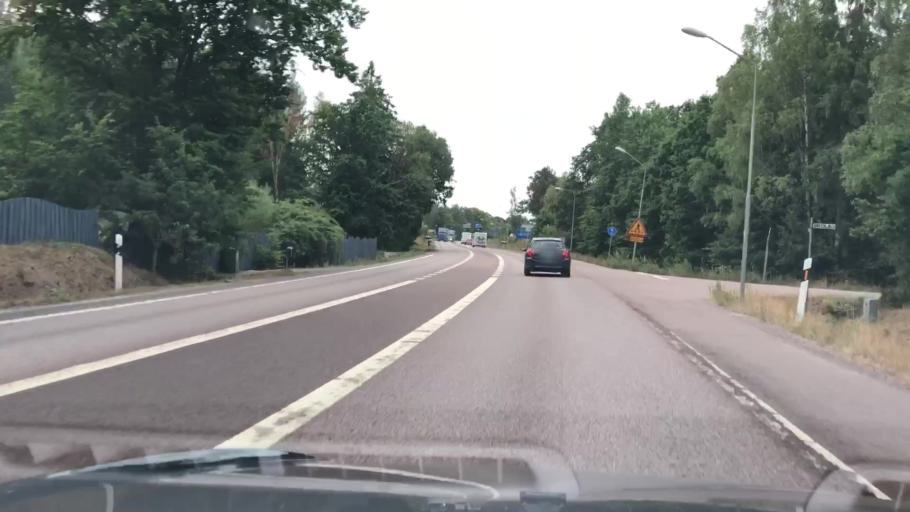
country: SE
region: Blekinge
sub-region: Karlskrona Kommun
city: Jaemjoe
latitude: 56.2633
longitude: 15.9506
